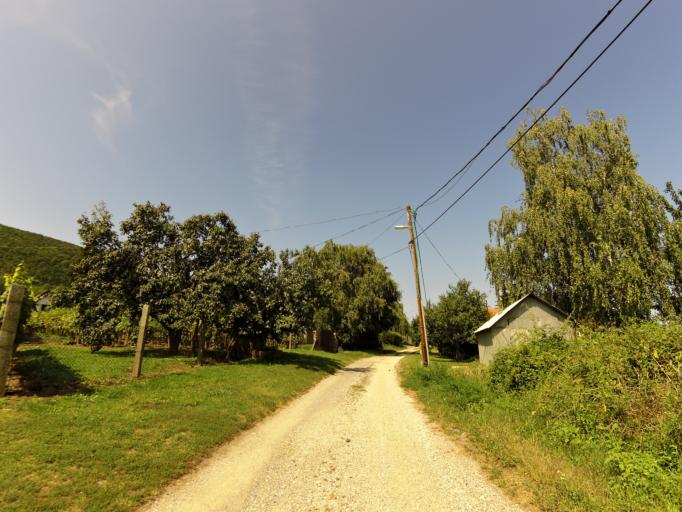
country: HU
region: Zala
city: Vonyarcvashegy
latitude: 46.8120
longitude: 17.3750
